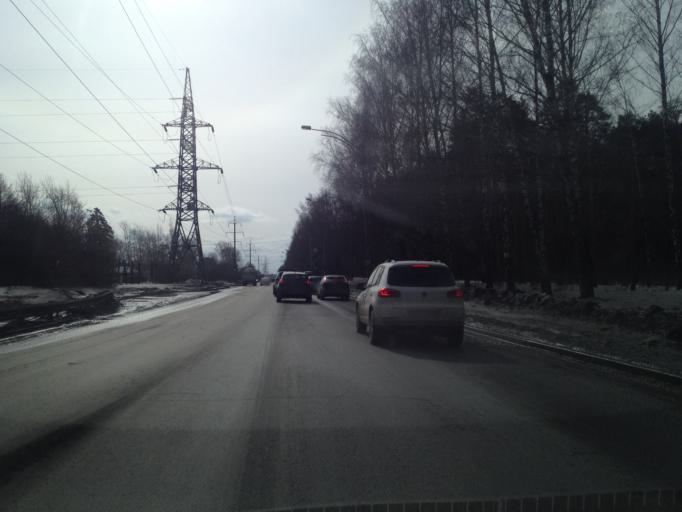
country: RU
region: Sverdlovsk
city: Sovkhoznyy
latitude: 56.7851
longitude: 60.5980
